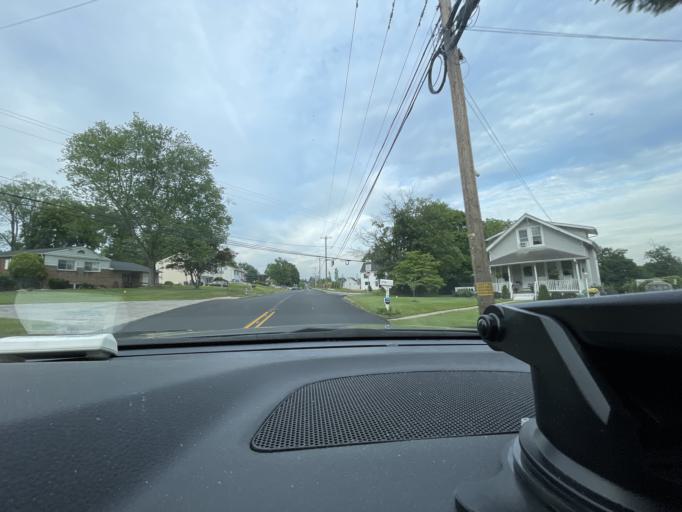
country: US
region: Pennsylvania
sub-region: Montgomery County
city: Plymouth Meeting
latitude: 40.1148
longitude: -75.3056
